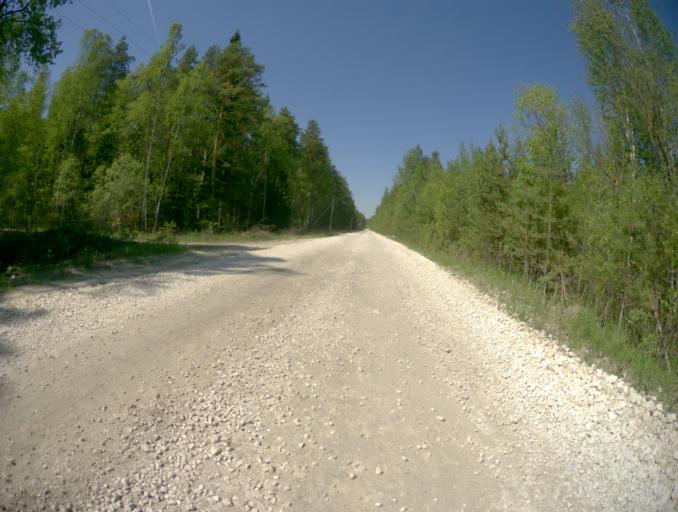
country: RU
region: Vladimir
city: Gusevskiy
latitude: 55.7207
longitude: 40.5883
